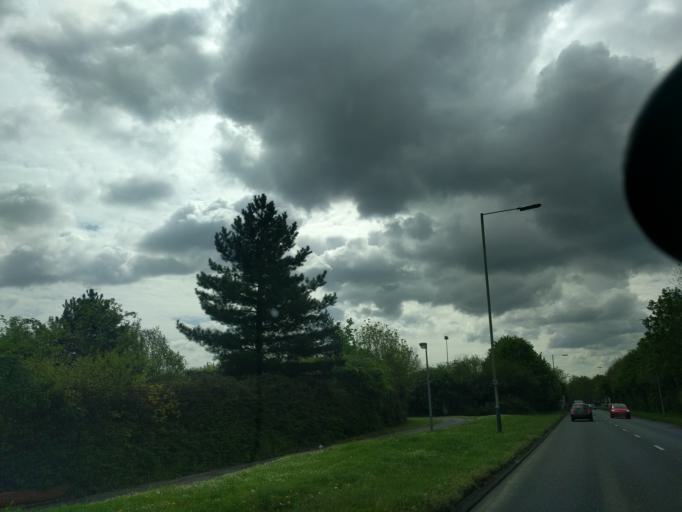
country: GB
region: England
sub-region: Wiltshire
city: Lydiard Tregoze
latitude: 51.5687
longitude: -1.8276
